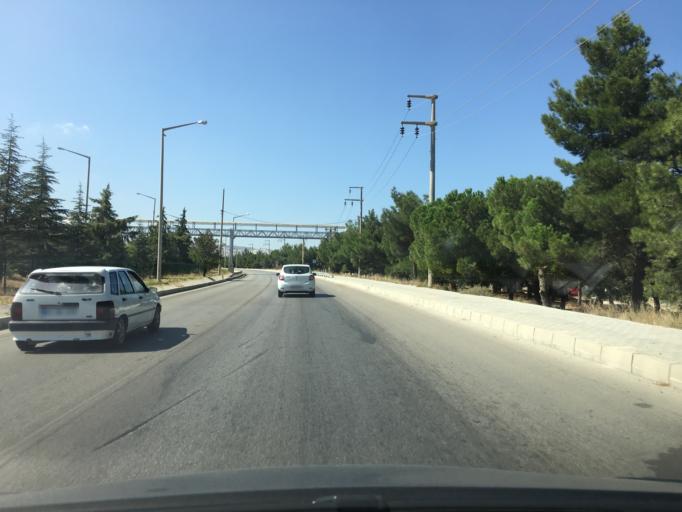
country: TR
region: Burdur
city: Burdur
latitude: 37.7284
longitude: 30.3029
